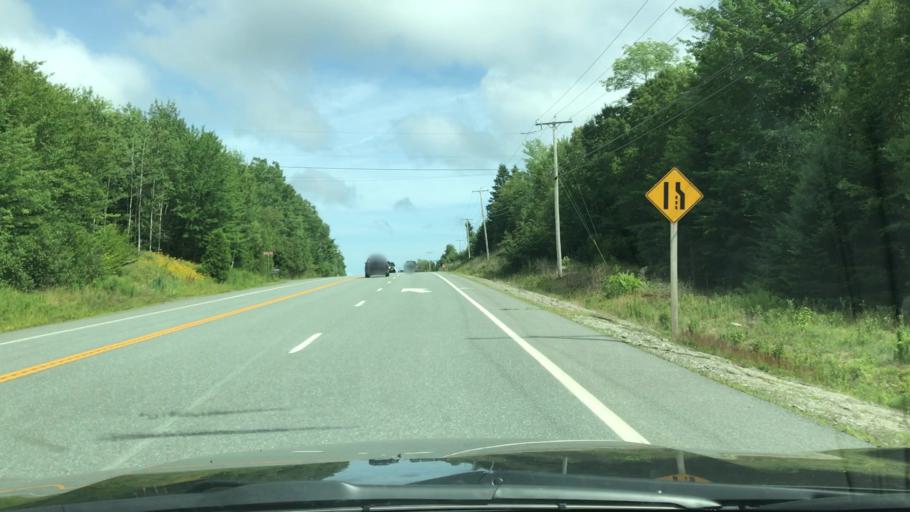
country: US
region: Maine
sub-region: Hancock County
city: Surry
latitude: 44.5473
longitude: -68.5235
